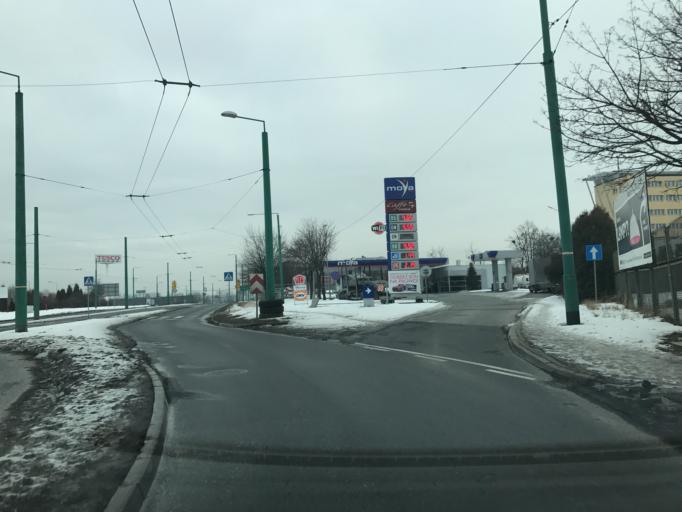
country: PL
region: Silesian Voivodeship
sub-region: Tychy
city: Cielmice
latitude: 50.1001
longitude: 19.0107
